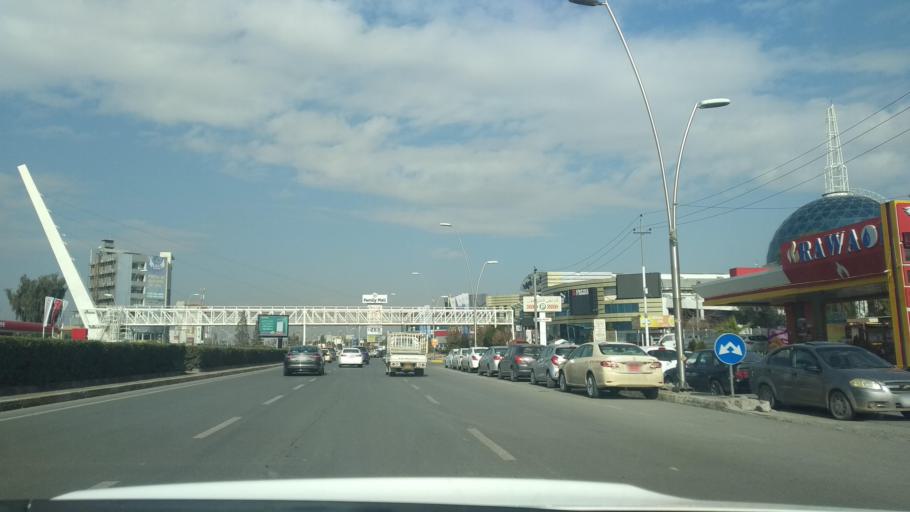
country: IQ
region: Arbil
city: Erbil
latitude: 36.2082
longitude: 44.0445
